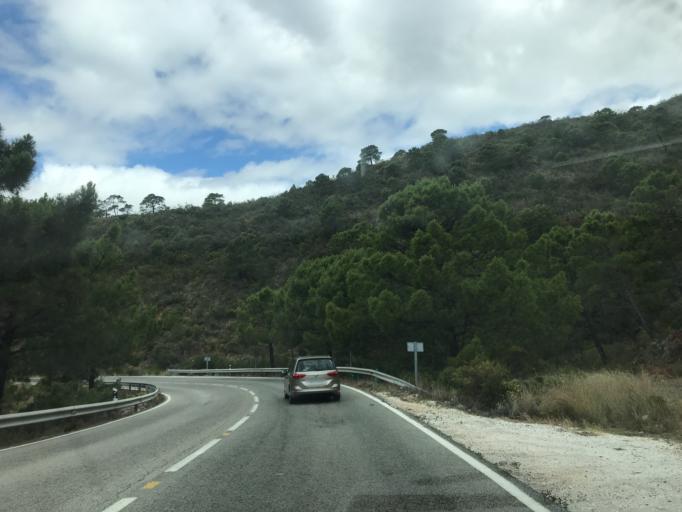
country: ES
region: Andalusia
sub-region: Provincia de Malaga
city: Benahavis
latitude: 36.5538
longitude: -5.0333
